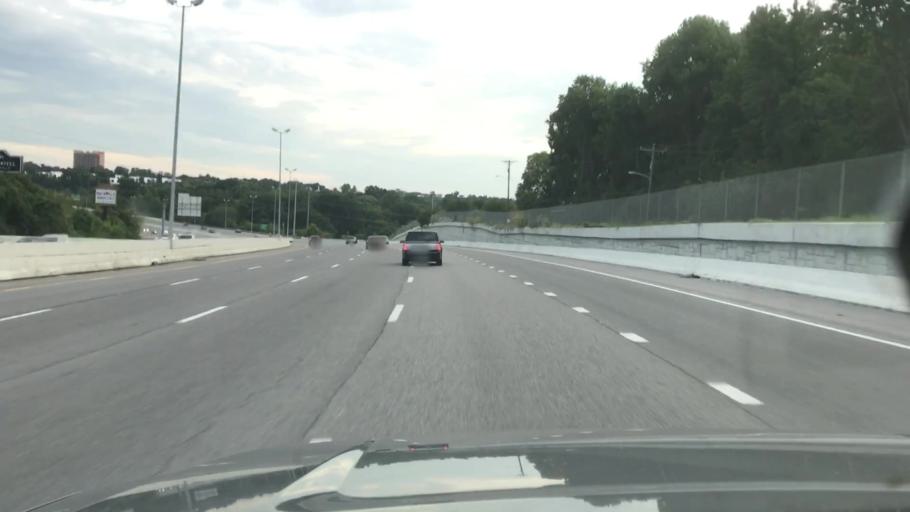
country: US
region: Tennessee
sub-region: Davidson County
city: Nashville
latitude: 36.1611
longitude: -86.6916
